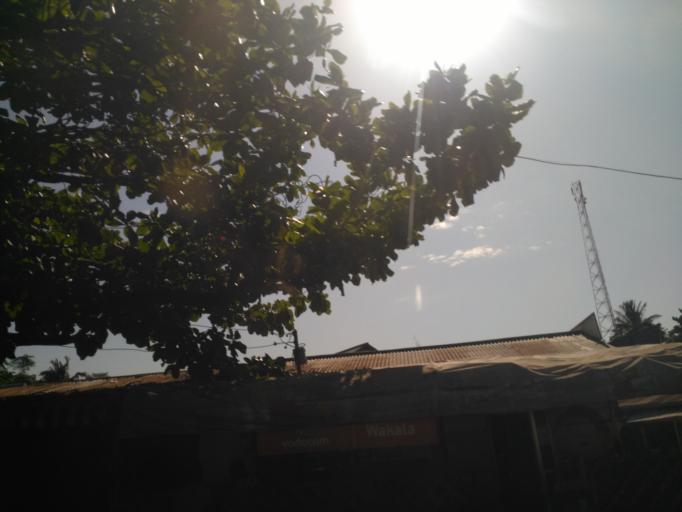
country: TZ
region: Mwanza
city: Mwanza
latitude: -2.4917
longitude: 32.8977
